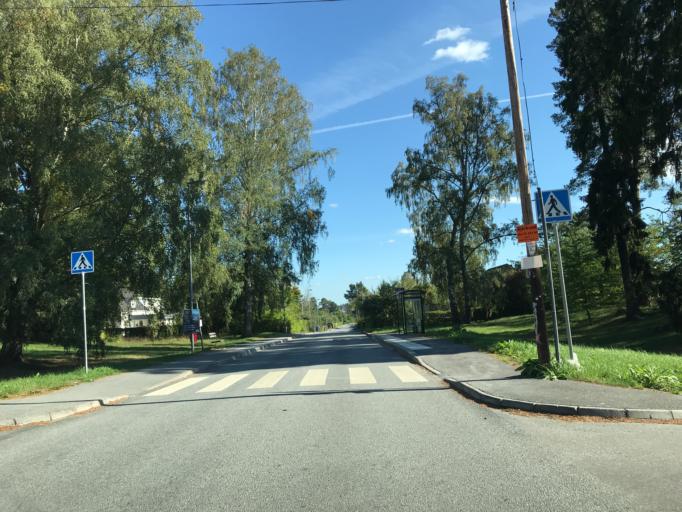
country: SE
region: Stockholm
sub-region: Sollentuna Kommun
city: Sollentuna
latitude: 59.4184
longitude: 17.9757
